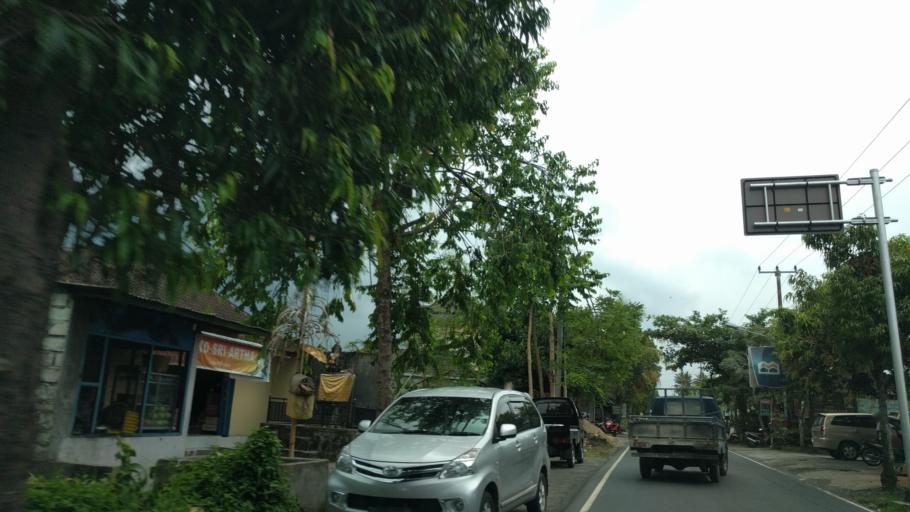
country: ID
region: Bali
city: Banjar Pande
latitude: -8.5183
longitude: 115.2398
